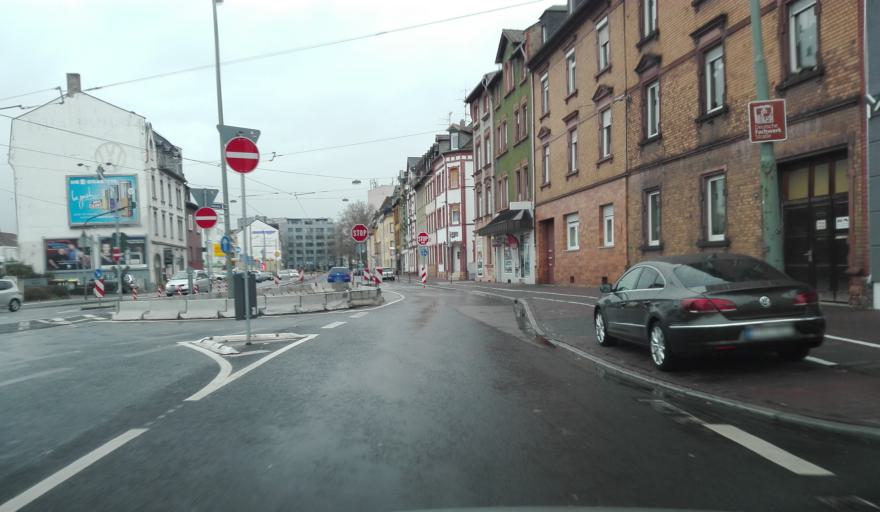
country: DE
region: Hesse
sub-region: Regierungsbezirk Darmstadt
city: Eschborn
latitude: 50.1017
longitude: 8.5603
